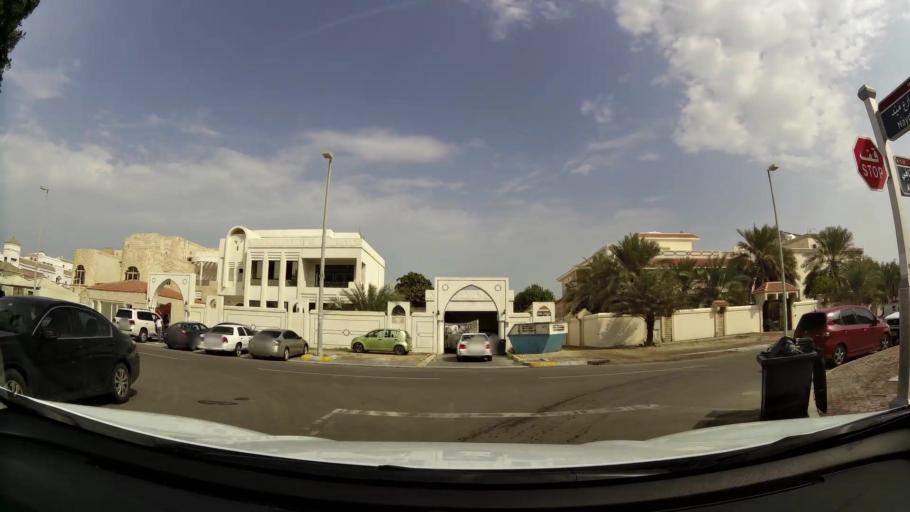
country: AE
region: Abu Dhabi
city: Abu Dhabi
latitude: 24.4408
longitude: 54.4300
